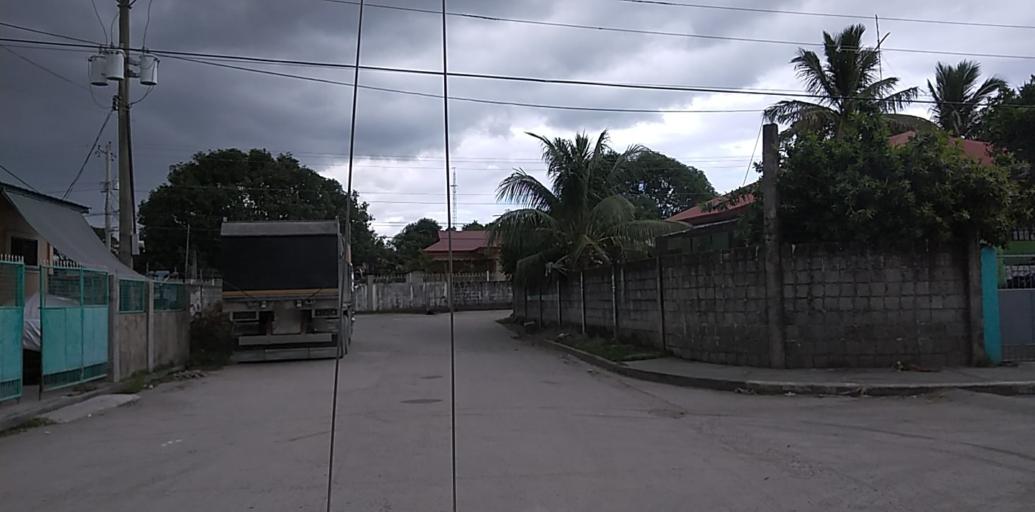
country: PH
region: Central Luzon
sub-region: Province of Pampanga
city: Pio
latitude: 15.0477
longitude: 120.5309
